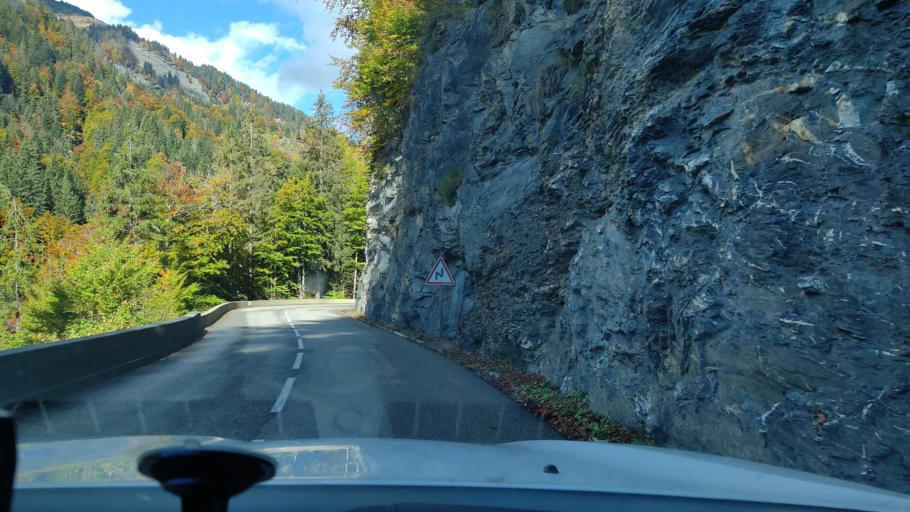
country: FR
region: Rhone-Alpes
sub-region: Departement de la Haute-Savoie
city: Praz-sur-Arly
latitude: 45.8309
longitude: 6.5091
